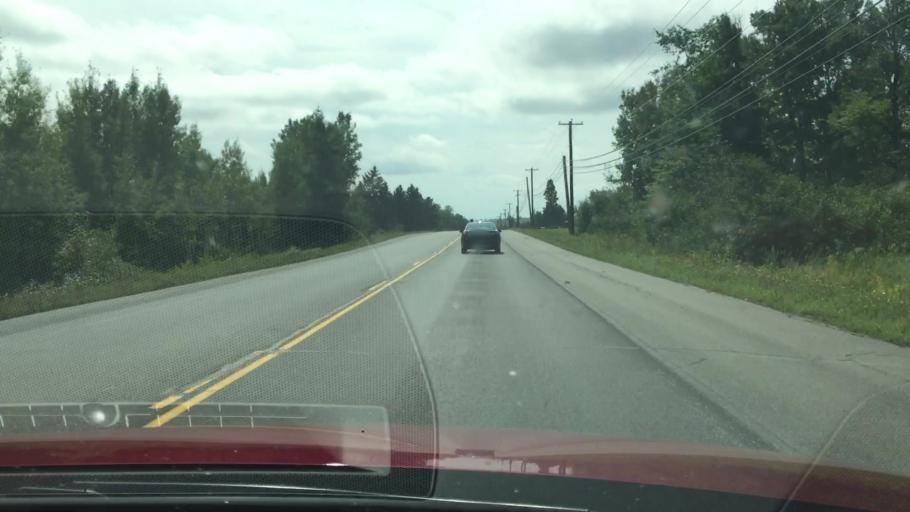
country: US
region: Maine
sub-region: Aroostook County
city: Houlton
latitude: 46.3293
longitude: -67.8417
